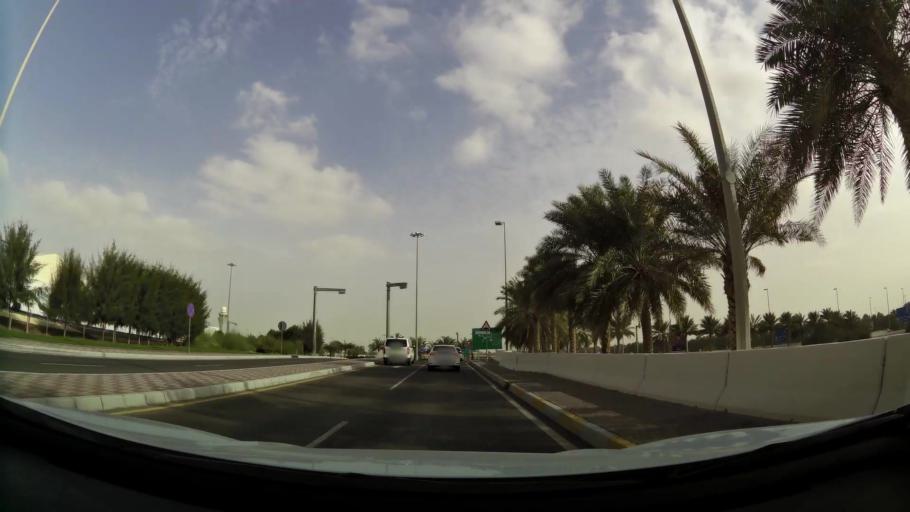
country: AE
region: Abu Dhabi
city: Abu Dhabi
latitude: 24.4267
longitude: 54.6418
